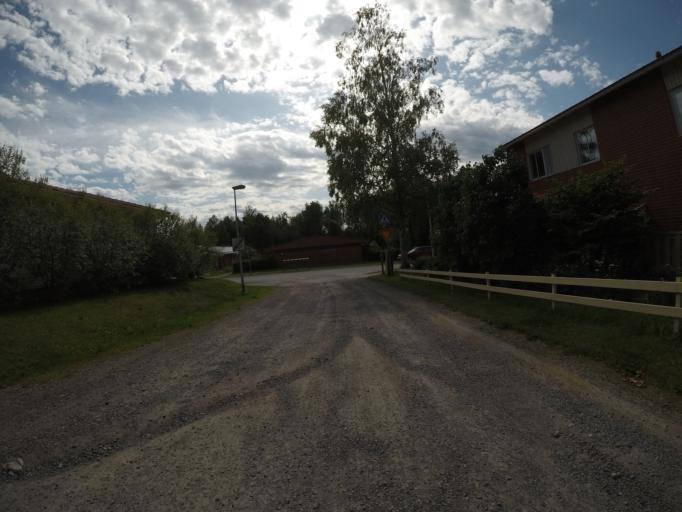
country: FI
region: Haeme
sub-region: Haemeenlinna
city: Haemeenlinna
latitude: 60.9838
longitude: 24.3955
